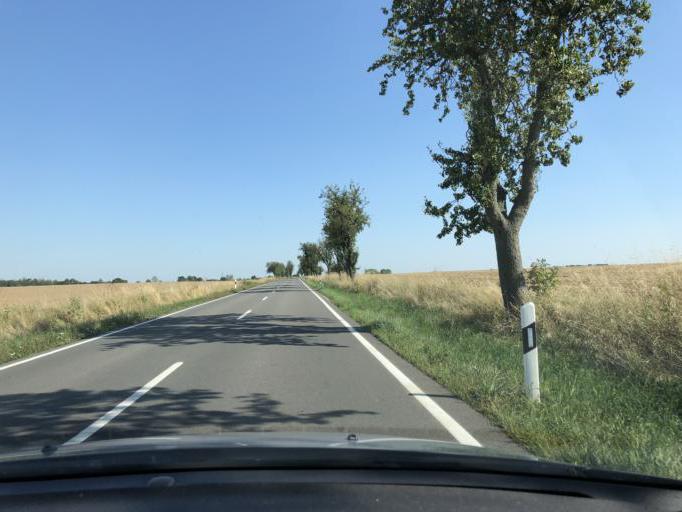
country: DE
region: Thuringia
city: Rastenberg
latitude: 51.1935
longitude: 11.4838
